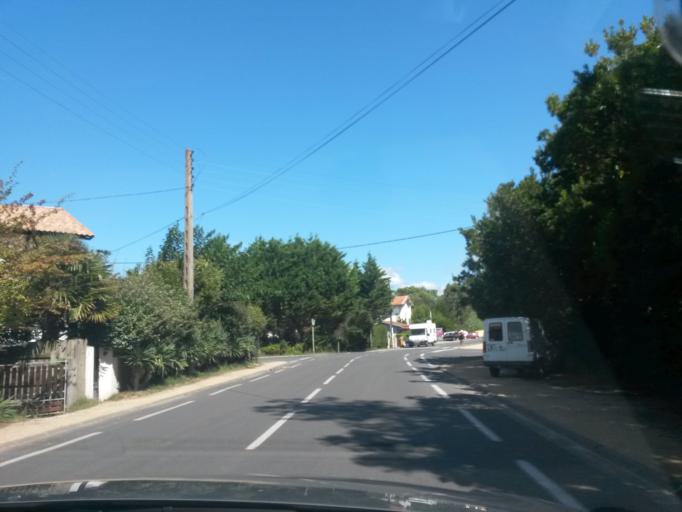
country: FR
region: Aquitaine
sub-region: Departement de la Gironde
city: Arcachon
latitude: 44.6563
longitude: -1.2445
